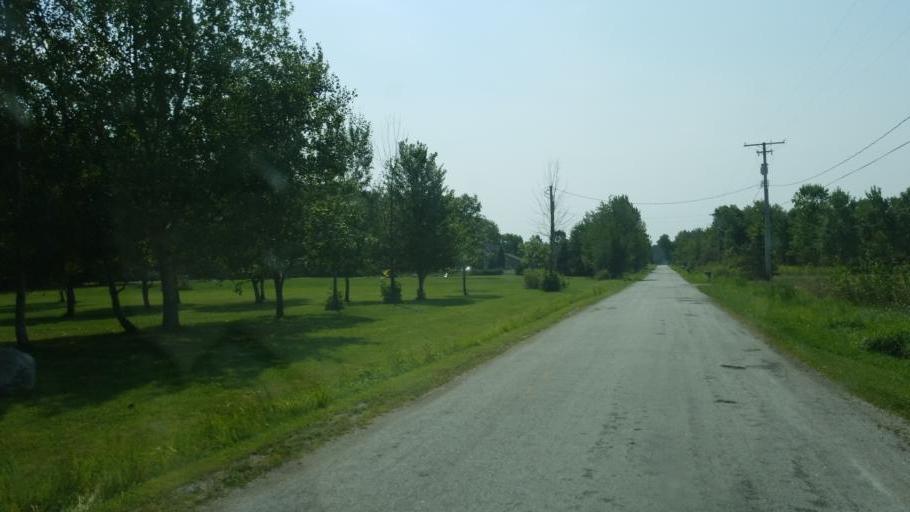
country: US
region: Ohio
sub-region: Ashtabula County
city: Orwell
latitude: 41.5902
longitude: -80.9923
